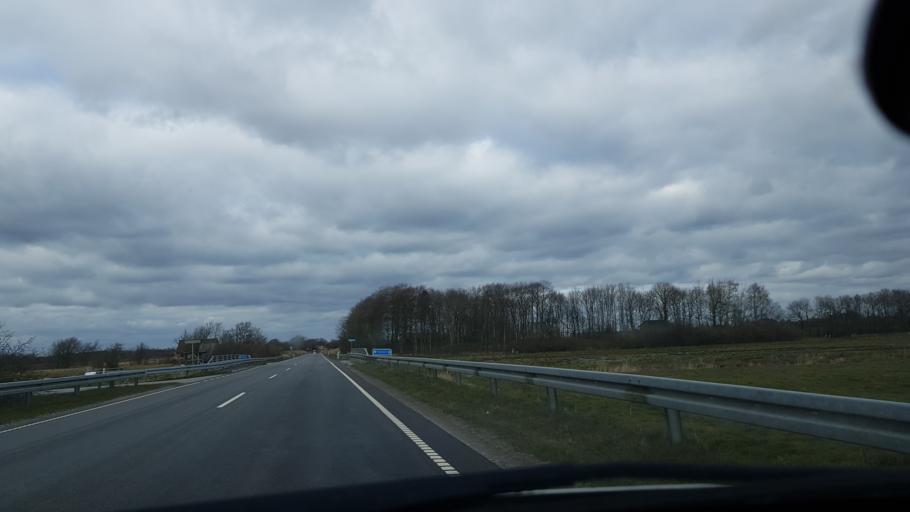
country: DK
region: South Denmark
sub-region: Vejen Kommune
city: Holsted
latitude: 55.4073
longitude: 8.8851
